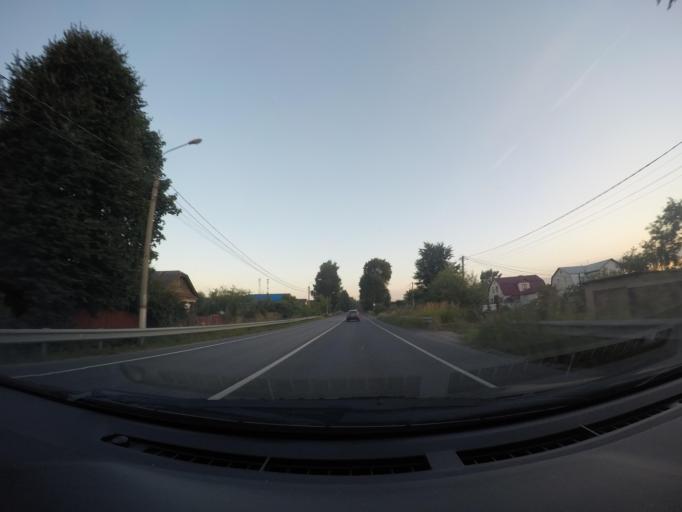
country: RU
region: Moskovskaya
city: Gzhel'
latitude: 55.6128
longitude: 38.3907
